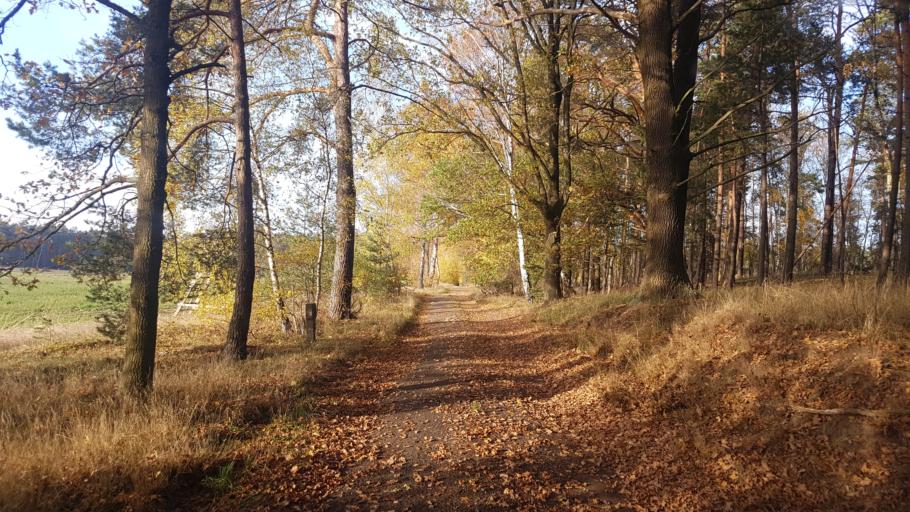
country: DE
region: Brandenburg
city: Calau
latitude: 51.6977
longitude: 13.9578
